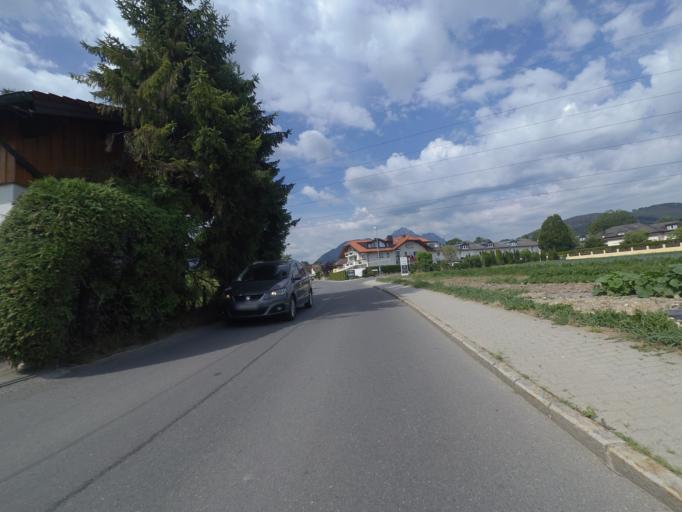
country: DE
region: Bavaria
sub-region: Upper Bavaria
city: Ainring
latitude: 47.7874
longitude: 12.9602
